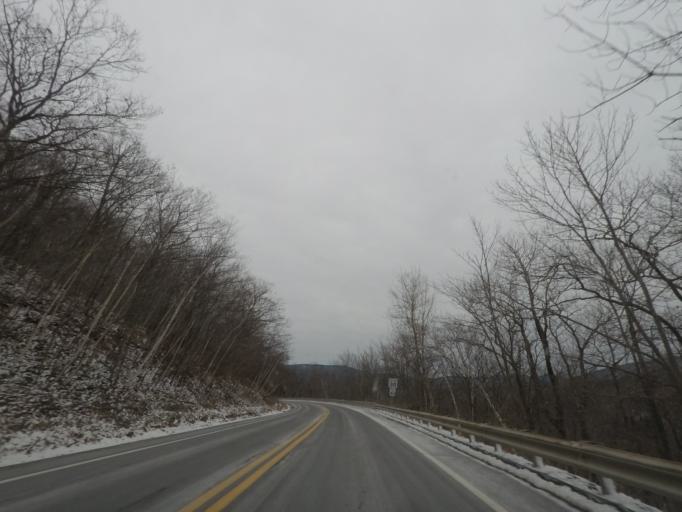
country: US
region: Massachusetts
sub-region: Berkshire County
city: Williamstown
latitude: 42.7204
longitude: -73.2653
